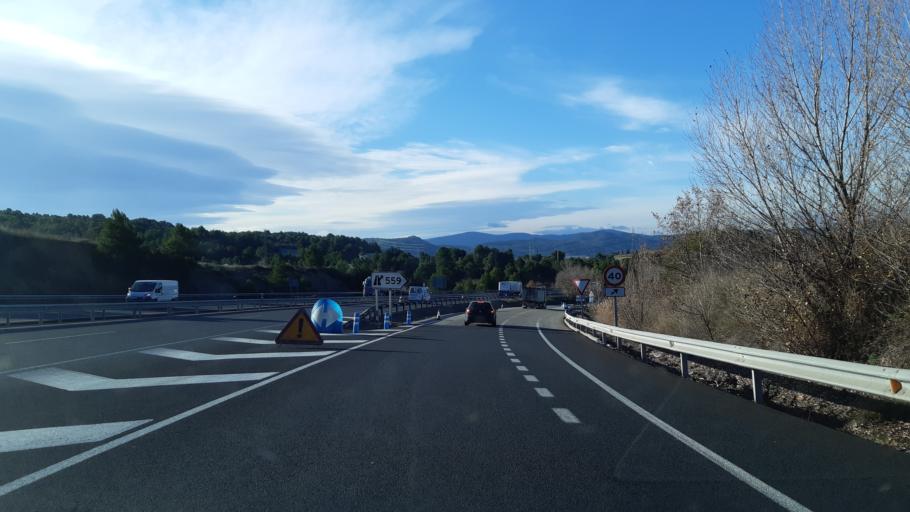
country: ES
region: Catalonia
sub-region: Provincia de Barcelona
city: Castelloli
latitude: 41.5892
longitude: 1.6783
